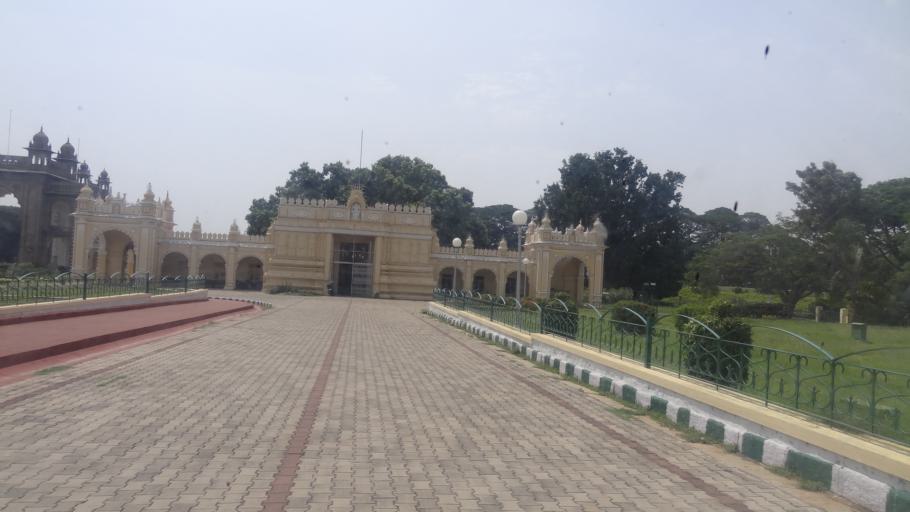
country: IN
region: Karnataka
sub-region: Mysore
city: Mysore
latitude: 12.3045
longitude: 76.6565
